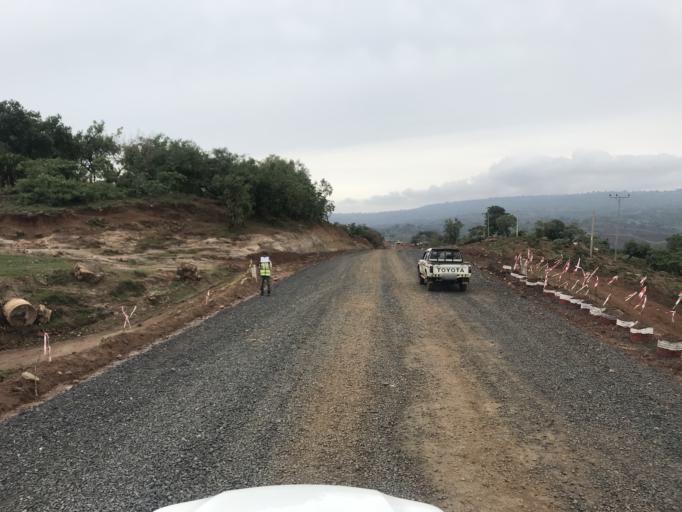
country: ET
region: Oromiya
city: Shambu
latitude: 10.0769
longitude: 36.8806
